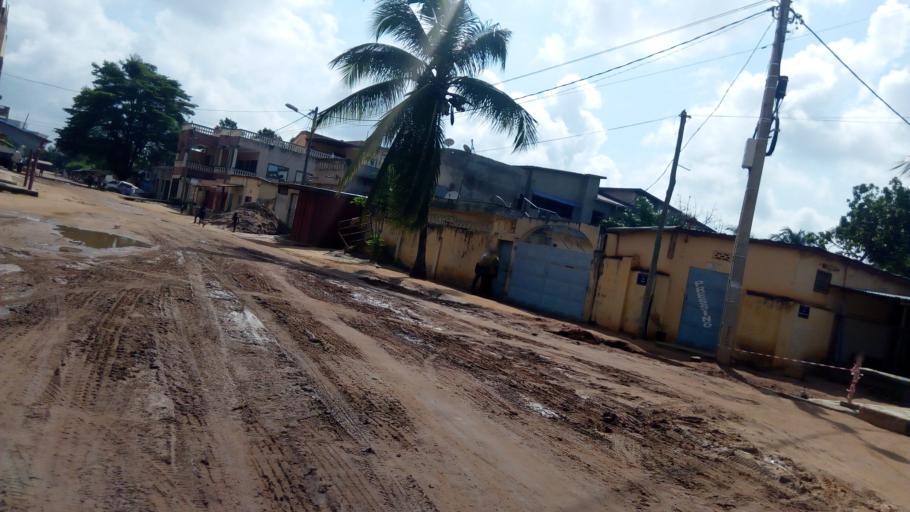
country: TG
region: Maritime
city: Lome
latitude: 6.1734
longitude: 1.1813
